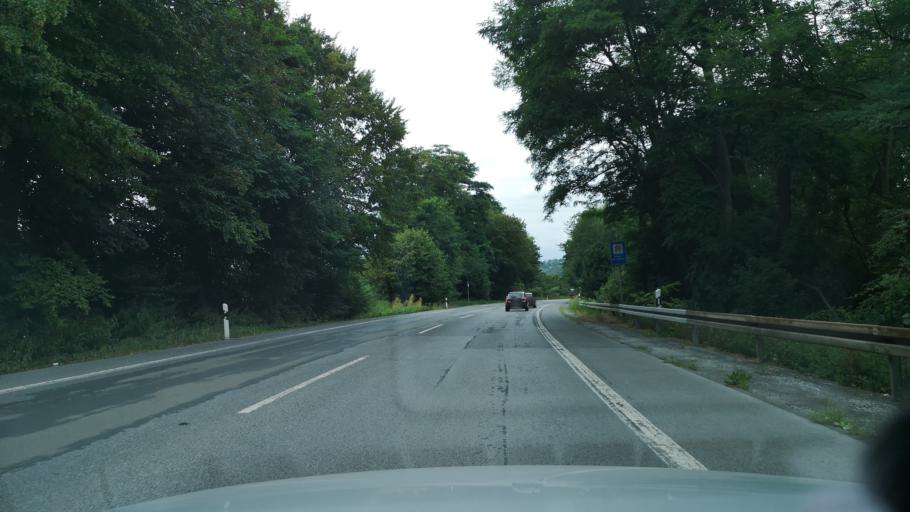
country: DE
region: North Rhine-Westphalia
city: Schwerte
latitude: 51.4086
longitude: 7.5188
